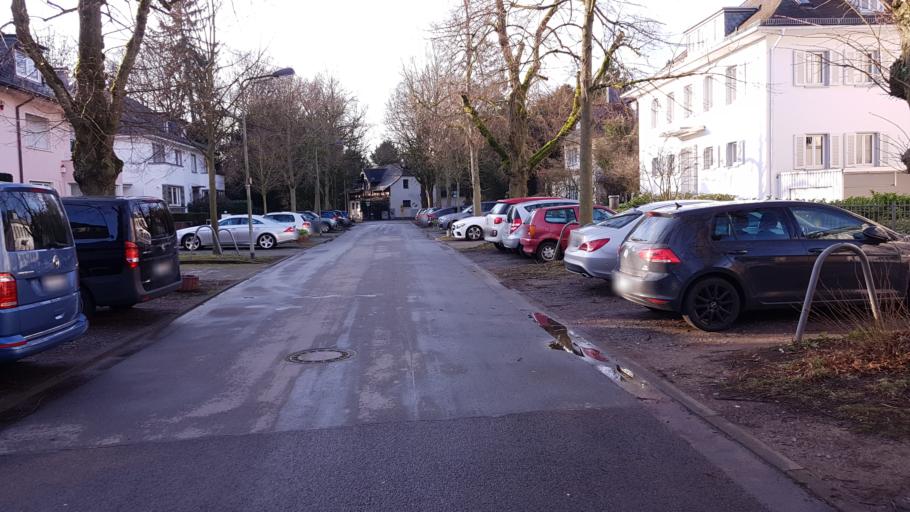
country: DE
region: Hesse
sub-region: Regierungsbezirk Darmstadt
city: Frankfurt am Main
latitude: 50.1298
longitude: 8.6622
